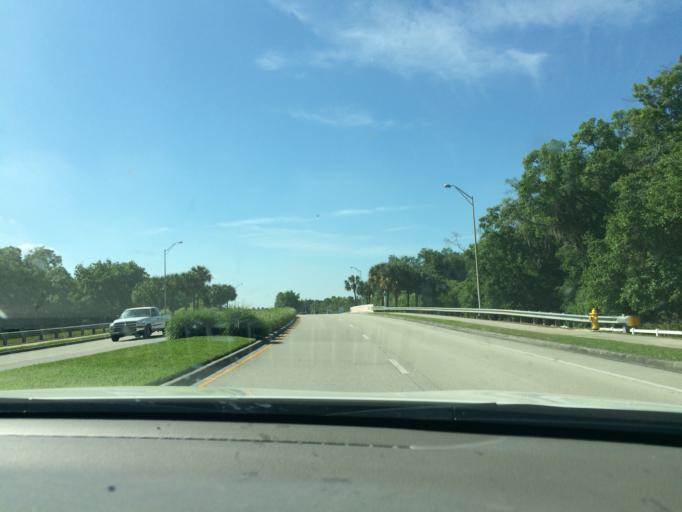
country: US
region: Florida
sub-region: Sarasota County
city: The Meadows
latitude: 27.4191
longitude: -82.3995
